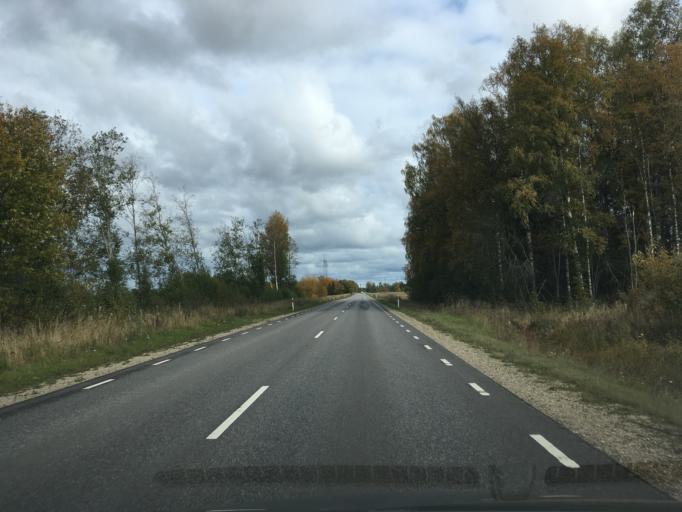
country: EE
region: Harju
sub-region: Anija vald
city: Kehra
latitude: 59.2473
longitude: 25.3064
